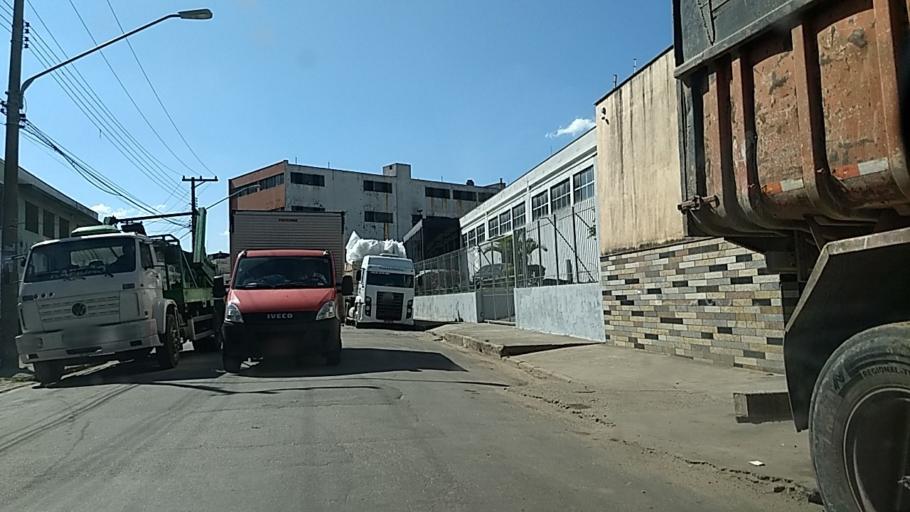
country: BR
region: Sao Paulo
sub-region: Sao Paulo
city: Sao Paulo
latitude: -23.5192
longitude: -46.6073
